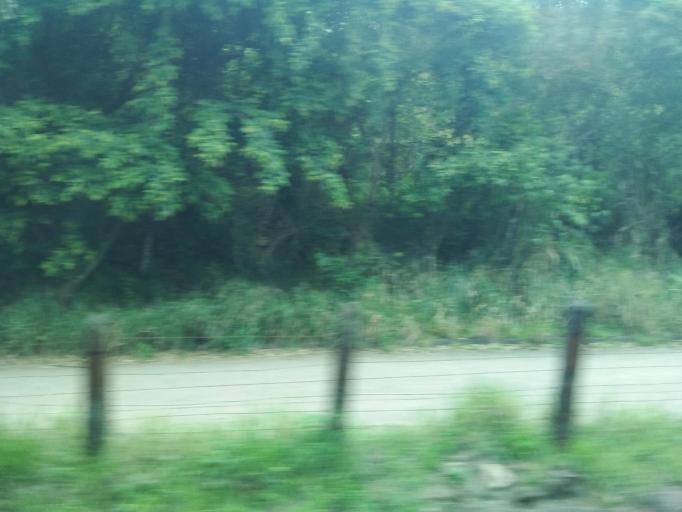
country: BR
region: Minas Gerais
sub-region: Nova Era
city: Nova Era
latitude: -19.7264
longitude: -42.9938
